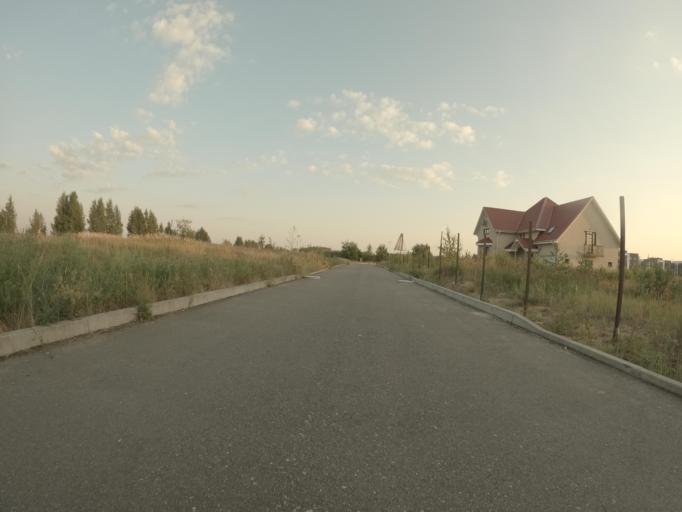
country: RU
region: Leningrad
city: Kirovsk
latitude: 59.8511
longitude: 30.9457
